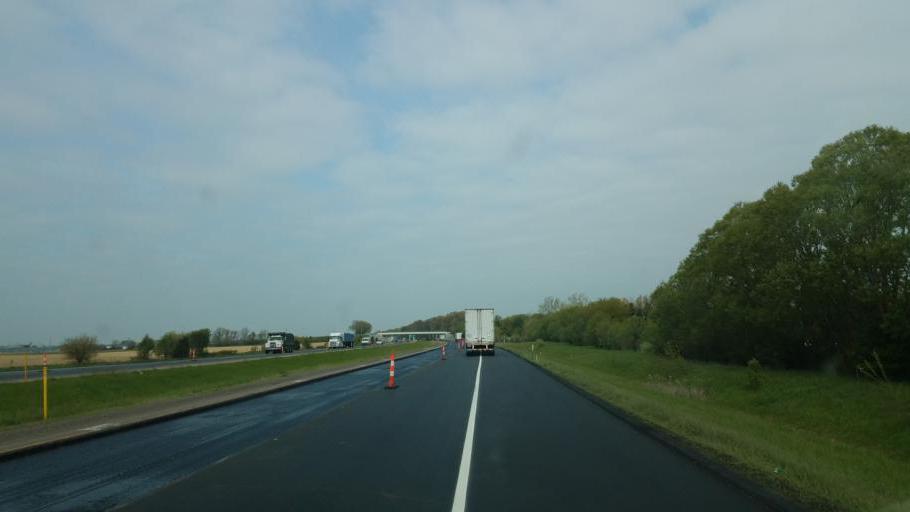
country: US
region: Indiana
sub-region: Saint Joseph County
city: Granger
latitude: 41.7332
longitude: -86.1031
